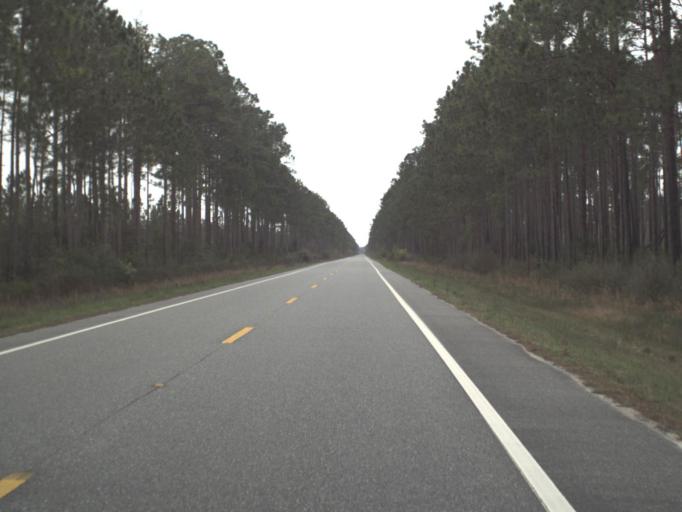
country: US
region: Florida
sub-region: Franklin County
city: Apalachicola
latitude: 29.8818
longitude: -84.9764
